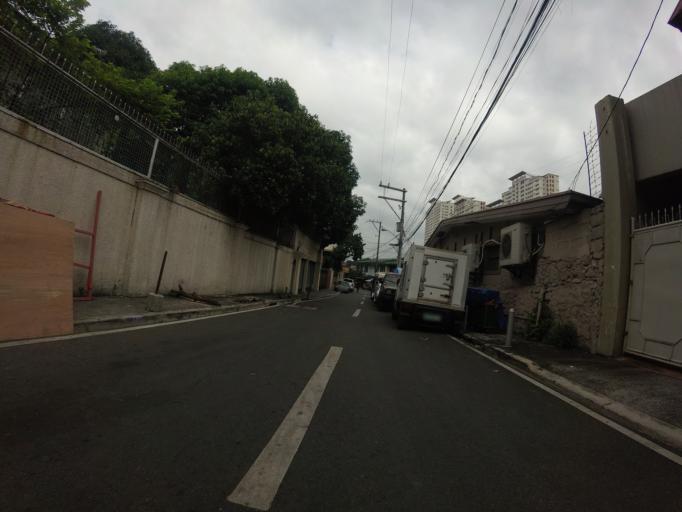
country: PH
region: Metro Manila
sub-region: San Juan
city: San Juan
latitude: 14.6086
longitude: 121.0300
